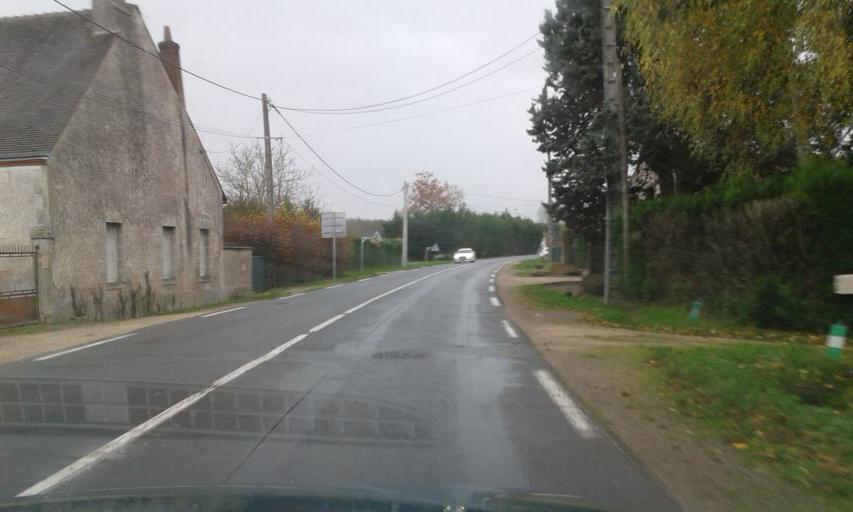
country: FR
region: Centre
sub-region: Departement du Loiret
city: Fay-aux-Loges
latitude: 47.9231
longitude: 2.1367
